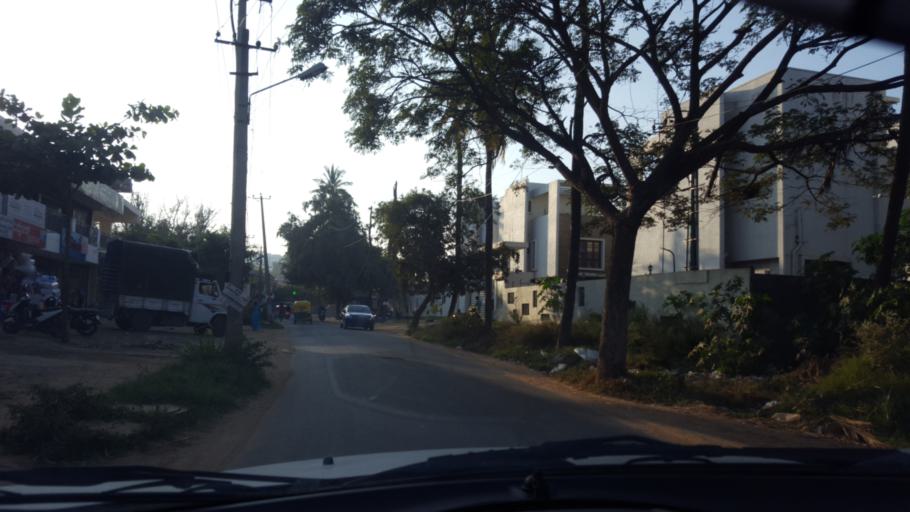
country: IN
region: Karnataka
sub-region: Bangalore Urban
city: Bangalore
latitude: 12.9393
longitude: 77.7320
